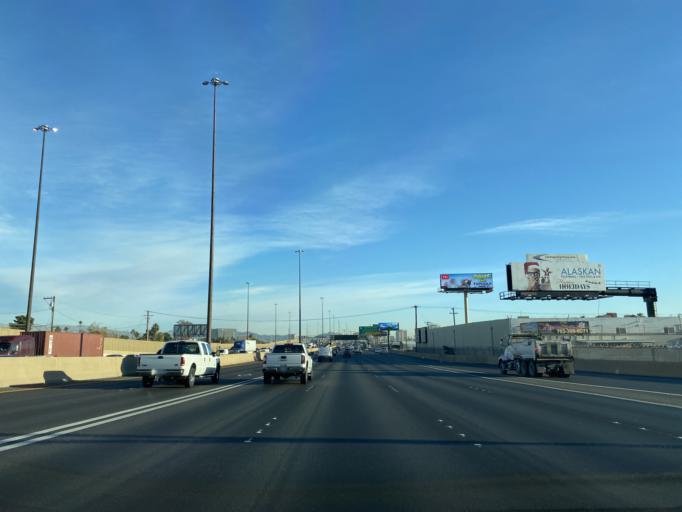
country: US
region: Nevada
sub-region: Clark County
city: Las Vegas
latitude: 36.1462
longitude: -115.1688
